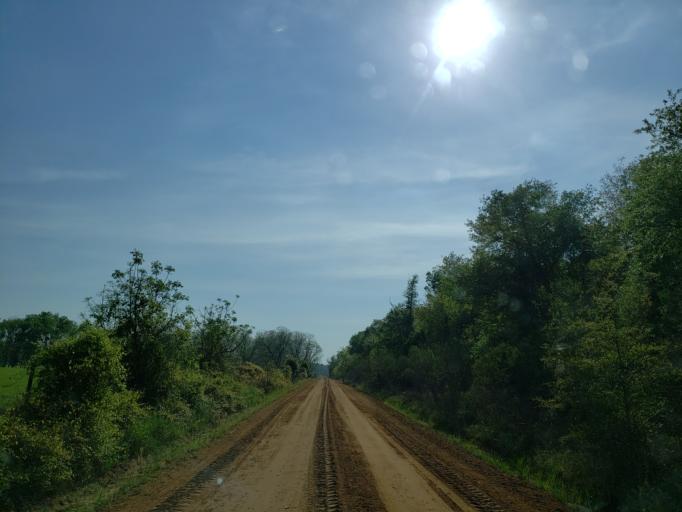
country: US
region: Georgia
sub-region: Dooly County
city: Vienna
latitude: 32.1086
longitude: -83.7778
